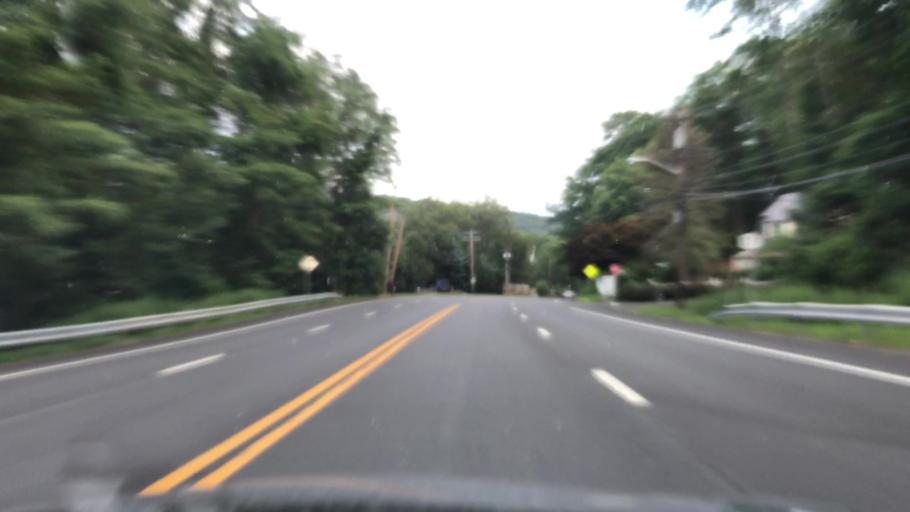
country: US
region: New York
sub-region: Rockland County
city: Sloatsburg
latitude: 41.2060
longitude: -74.1851
